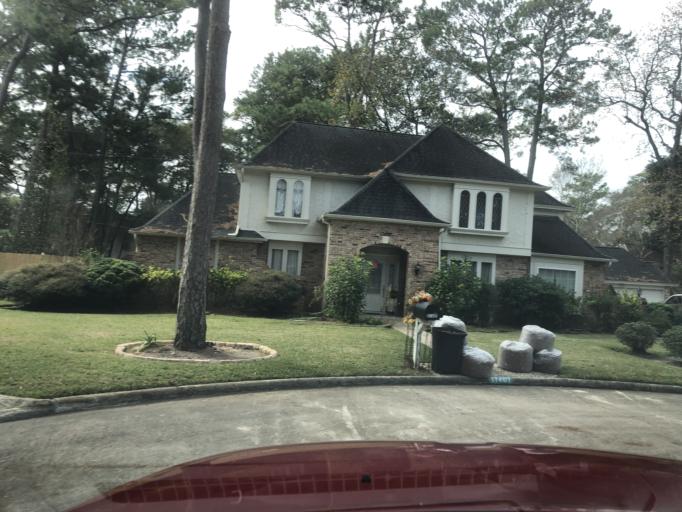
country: US
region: Texas
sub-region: Harris County
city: Spring
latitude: 30.0175
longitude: -95.4616
